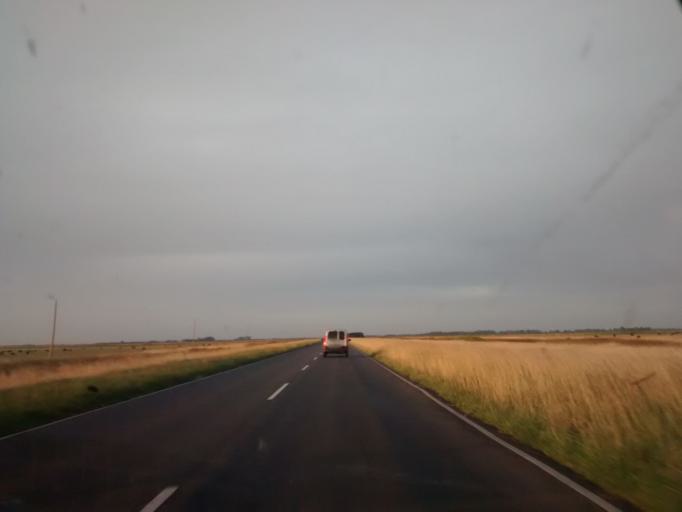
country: AR
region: Buenos Aires
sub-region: Partido de General Belgrano
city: General Belgrano
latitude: -35.9328
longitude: -58.6199
